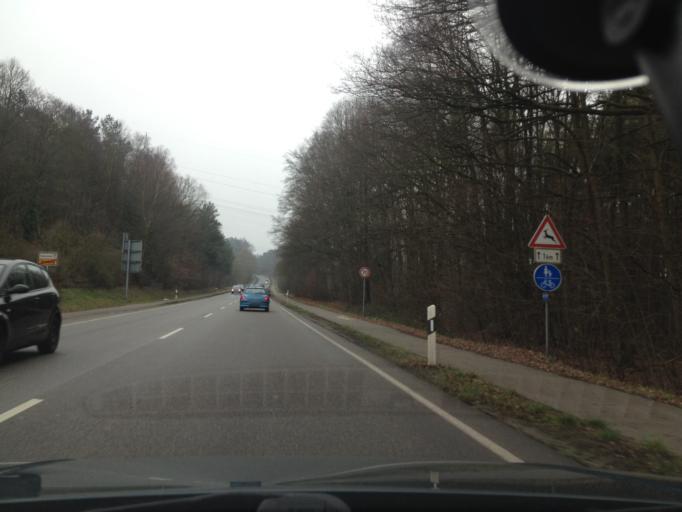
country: DE
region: Saarland
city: Homburg
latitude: 49.3029
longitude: 7.3287
